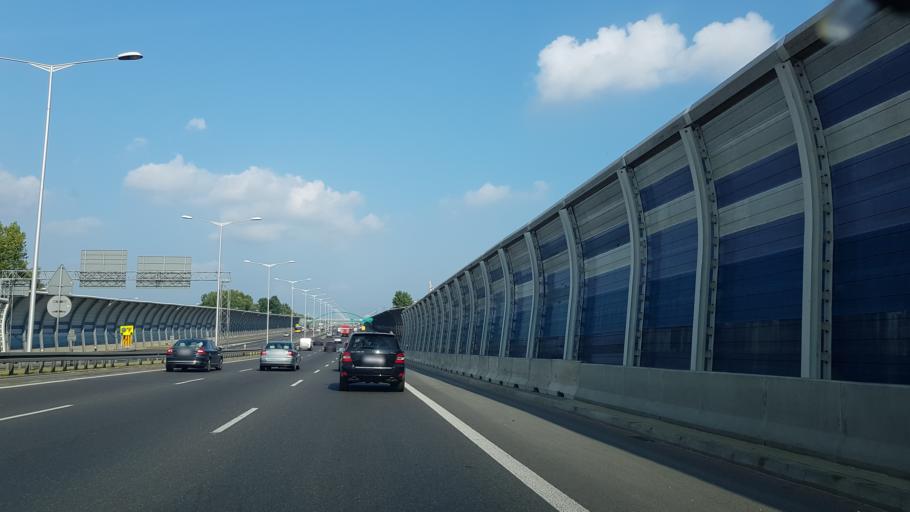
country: PL
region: Masovian Voivodeship
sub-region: Warszawa
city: Targowek
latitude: 52.2999
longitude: 21.0351
